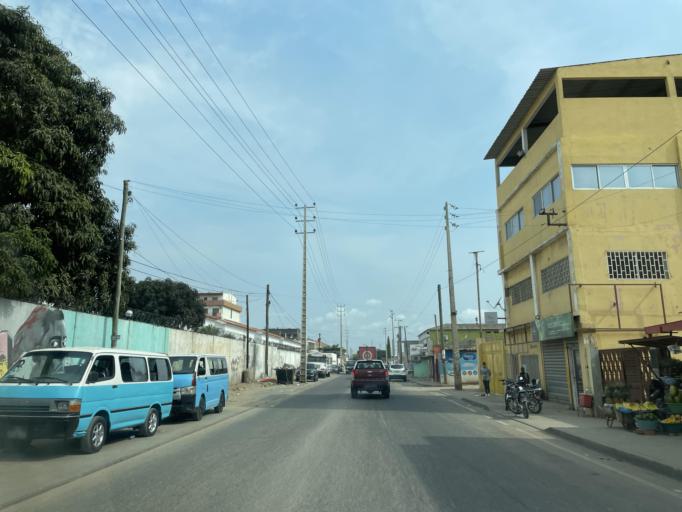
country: AO
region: Luanda
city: Luanda
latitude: -8.8970
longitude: 13.1905
